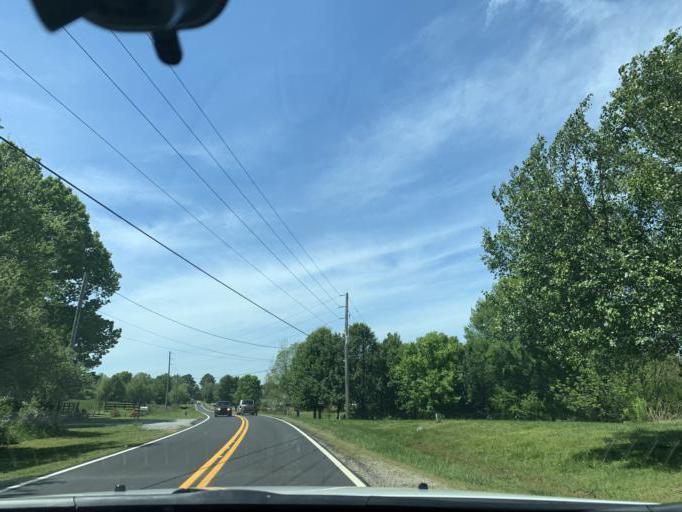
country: US
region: Georgia
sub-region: Forsyth County
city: Cumming
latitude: 34.2594
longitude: -84.0288
